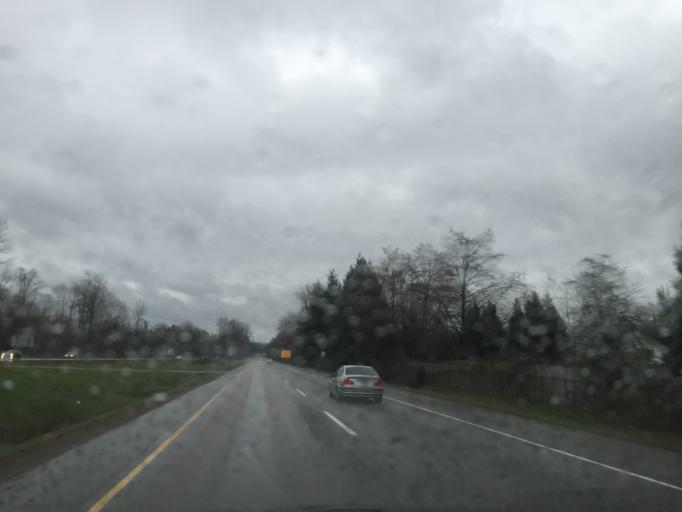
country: CA
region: British Columbia
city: Walnut Grove
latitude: 49.1534
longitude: -122.6290
